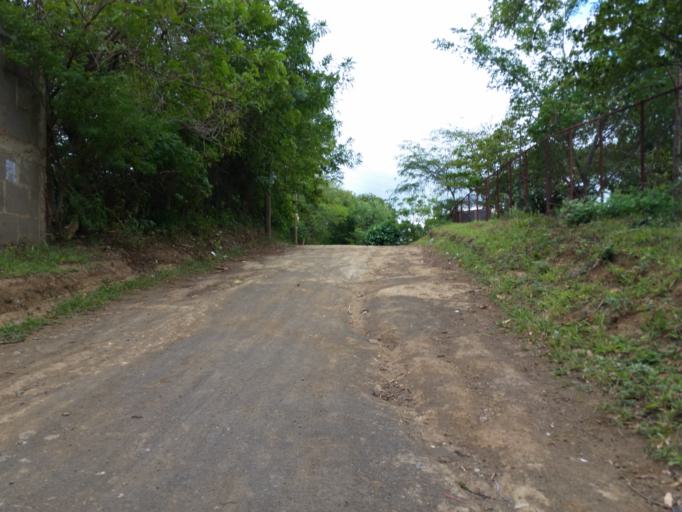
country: NI
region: Managua
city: Managua
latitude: 12.0858
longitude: -86.2524
